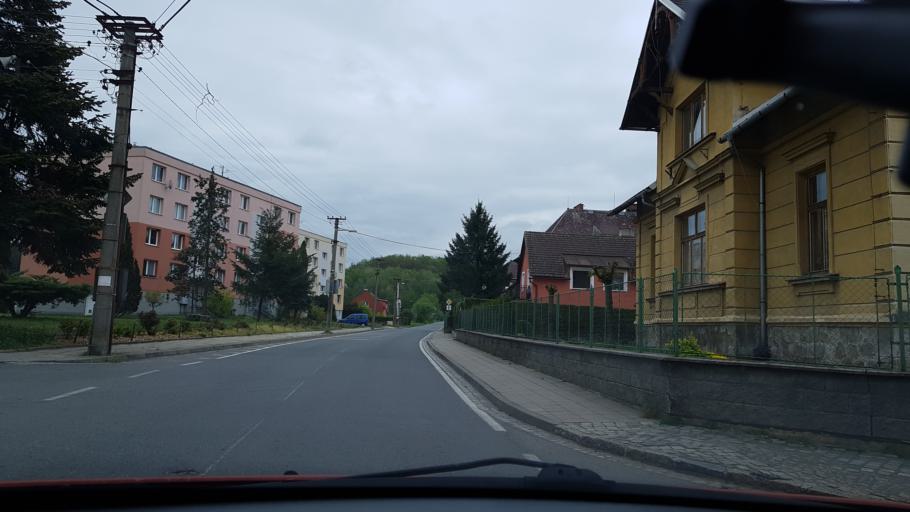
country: CZ
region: Olomoucky
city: Vidnava
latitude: 50.3716
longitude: 17.1879
